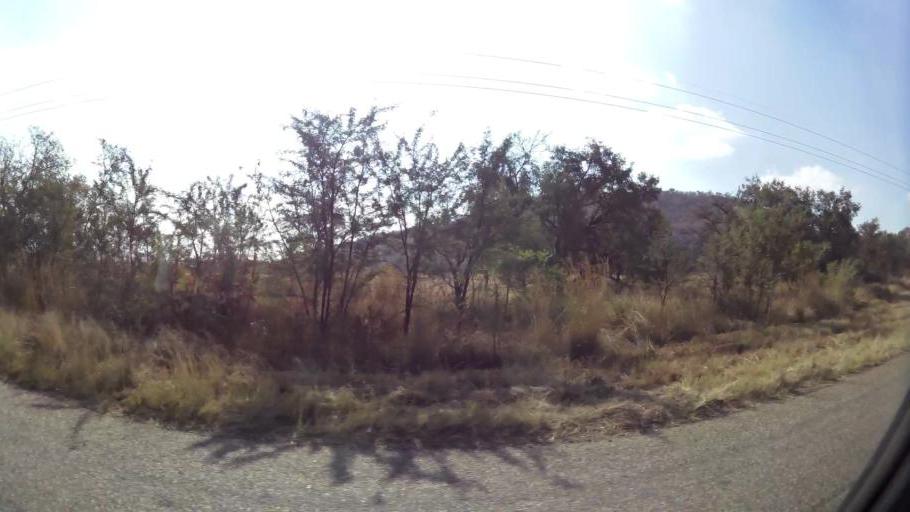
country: ZA
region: North-West
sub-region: Bojanala Platinum District Municipality
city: Rustenburg
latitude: -25.6324
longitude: 27.1764
